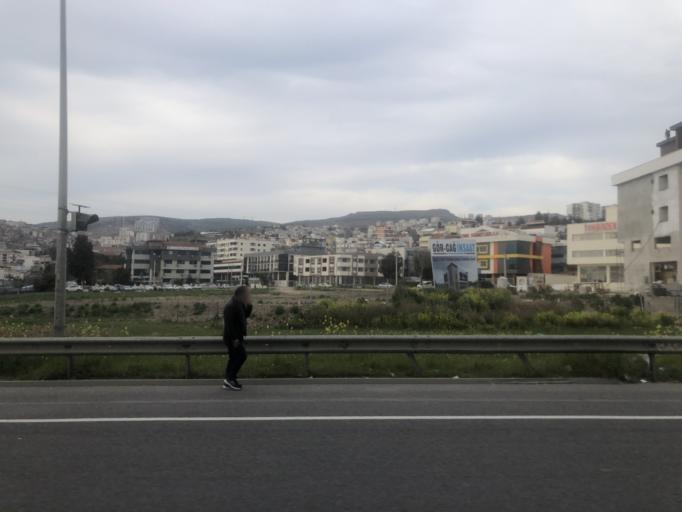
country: TR
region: Izmir
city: Karsiyaka
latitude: 38.4867
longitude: 27.0773
